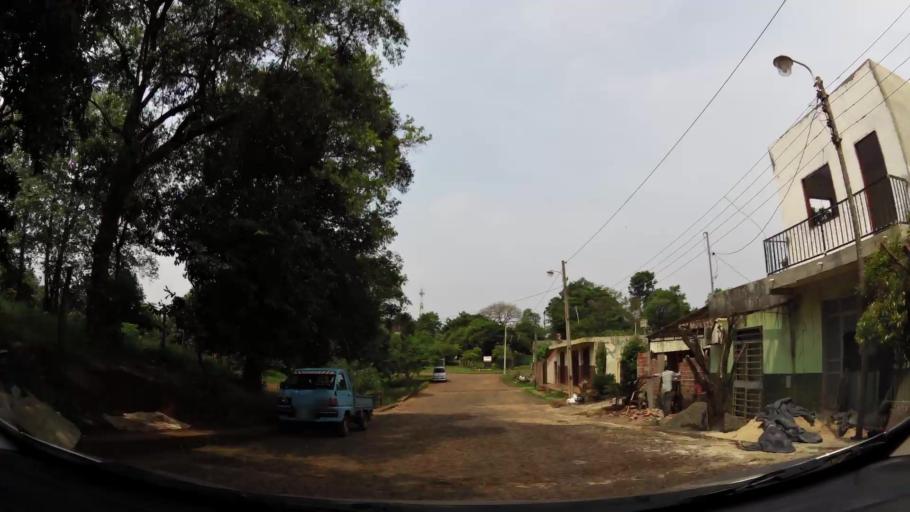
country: PY
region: Alto Parana
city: Presidente Franco
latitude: -25.5458
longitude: -54.6253
